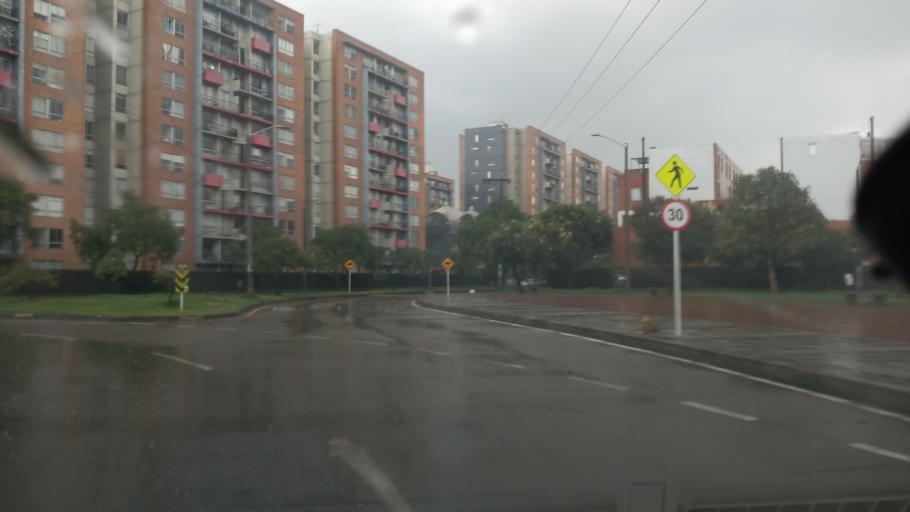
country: CO
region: Bogota D.C.
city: Bogota
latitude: 4.6440
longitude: -74.1283
